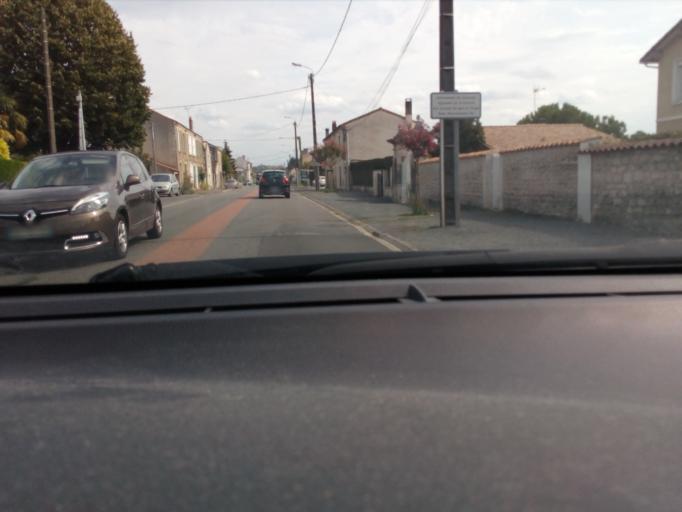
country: FR
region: Poitou-Charentes
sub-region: Departement de la Charente
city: Saint-Yrieix-sur-Charente
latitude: 45.6703
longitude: 0.1161
